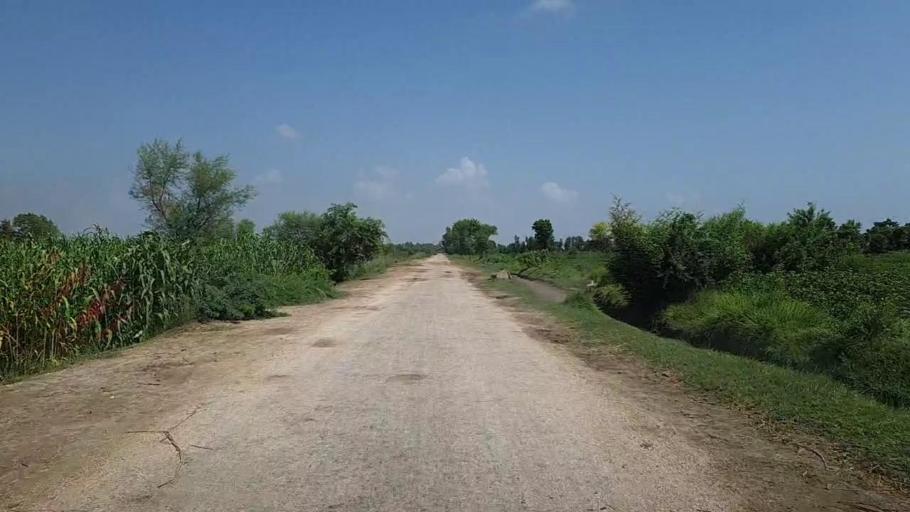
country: PK
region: Sindh
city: Bhiria
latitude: 26.8725
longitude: 68.2526
